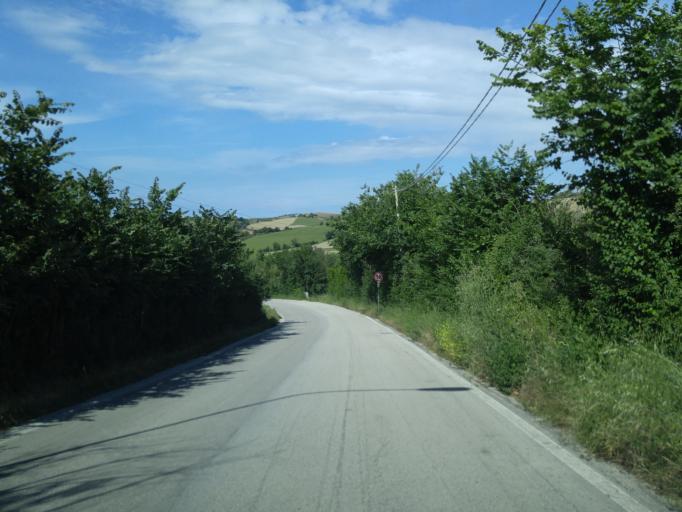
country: IT
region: The Marches
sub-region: Provincia di Pesaro e Urbino
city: San Costanzo
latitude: 43.7807
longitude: 13.0391
